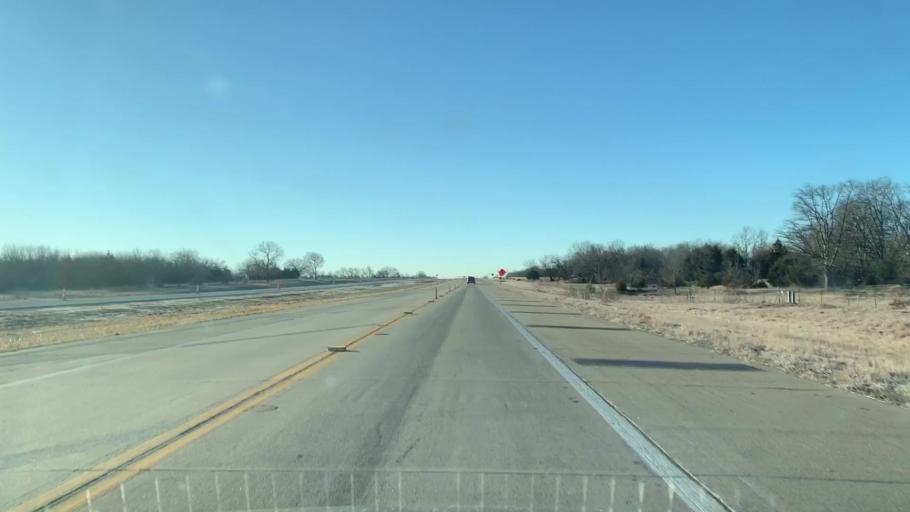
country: US
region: Kansas
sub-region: Bourbon County
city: Fort Scott
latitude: 37.7569
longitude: -94.7051
